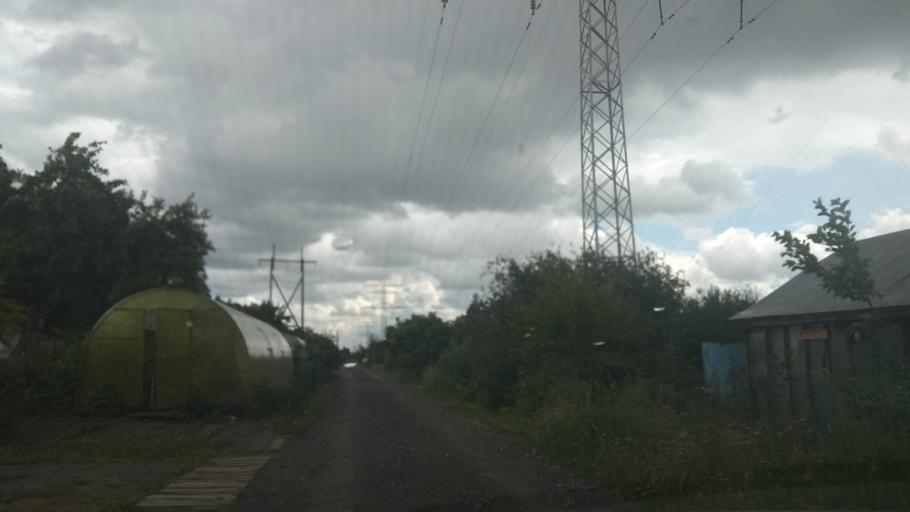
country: RU
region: Sverdlovsk
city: Verkhnyaya Pyshma
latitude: 56.9194
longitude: 60.5774
